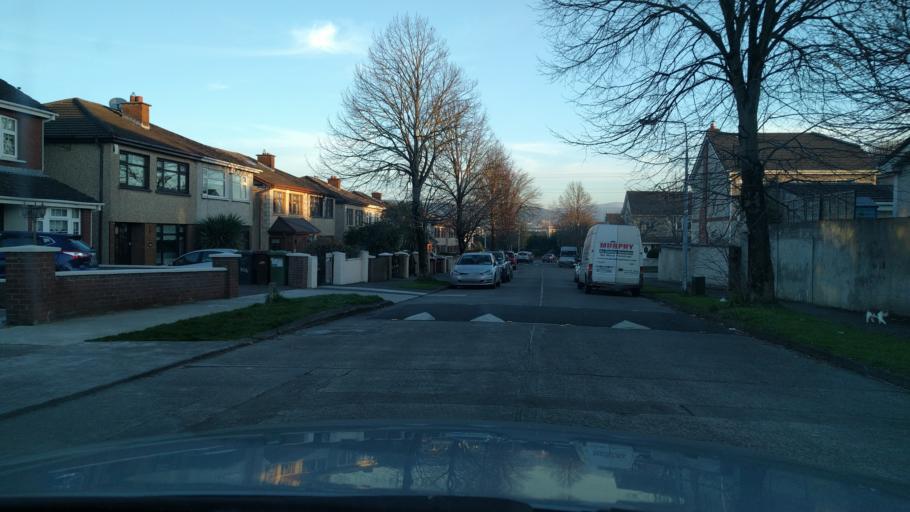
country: IE
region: Leinster
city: Tallaght
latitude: 53.2985
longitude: -6.3826
